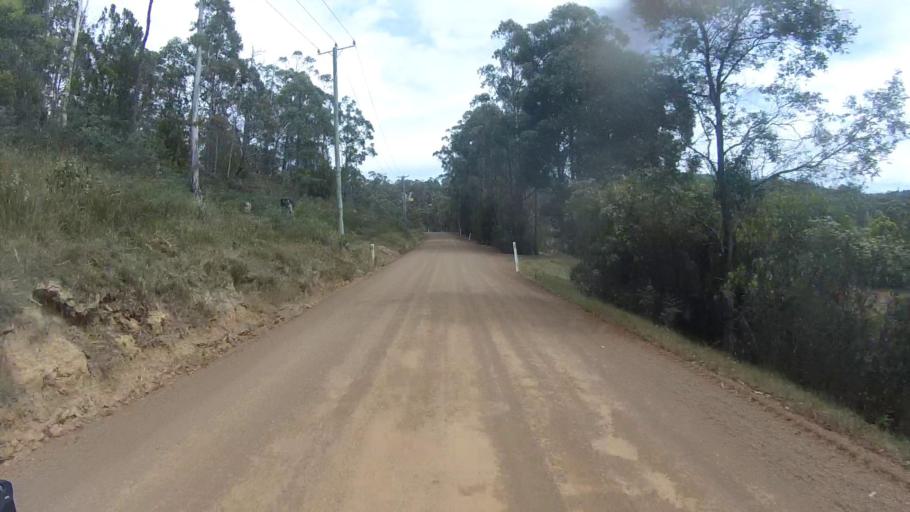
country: AU
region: Tasmania
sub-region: Sorell
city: Sorell
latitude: -42.7342
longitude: 147.7637
